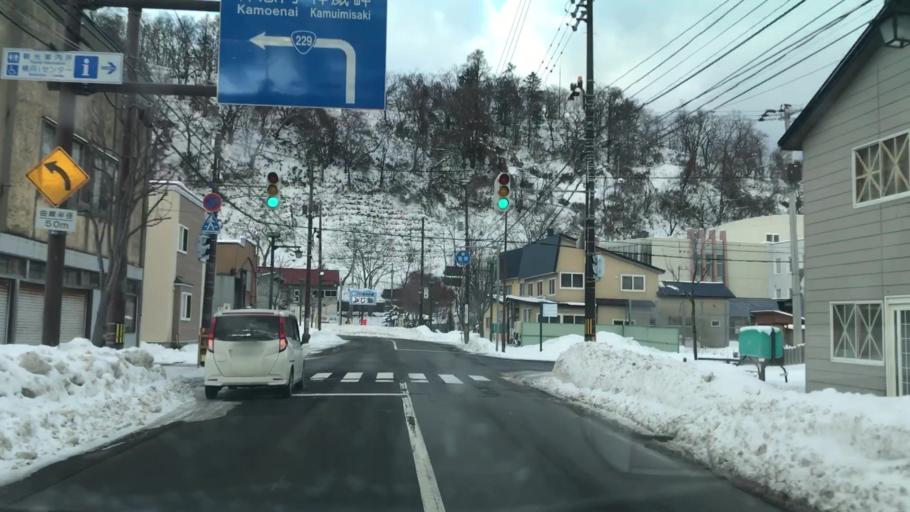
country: JP
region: Hokkaido
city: Yoichi
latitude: 43.2977
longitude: 140.5985
